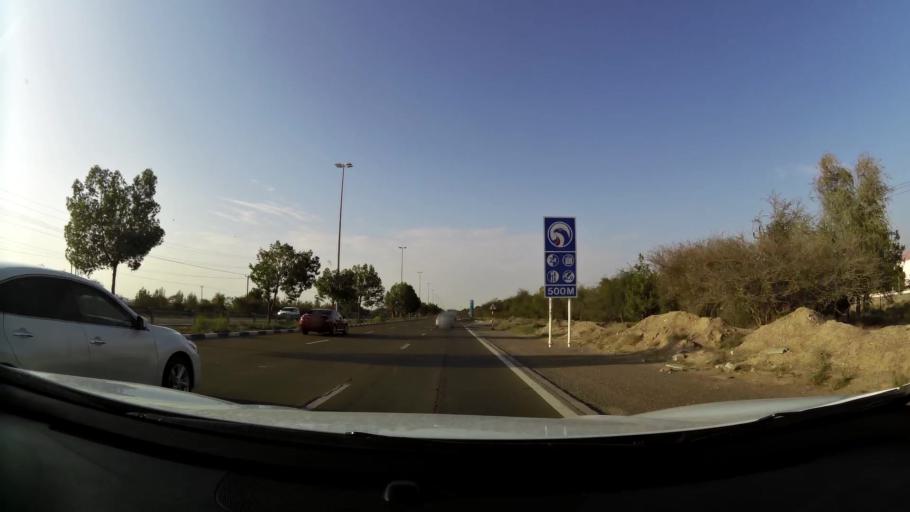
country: AE
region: Abu Dhabi
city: Al Ain
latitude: 24.1196
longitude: 55.8234
